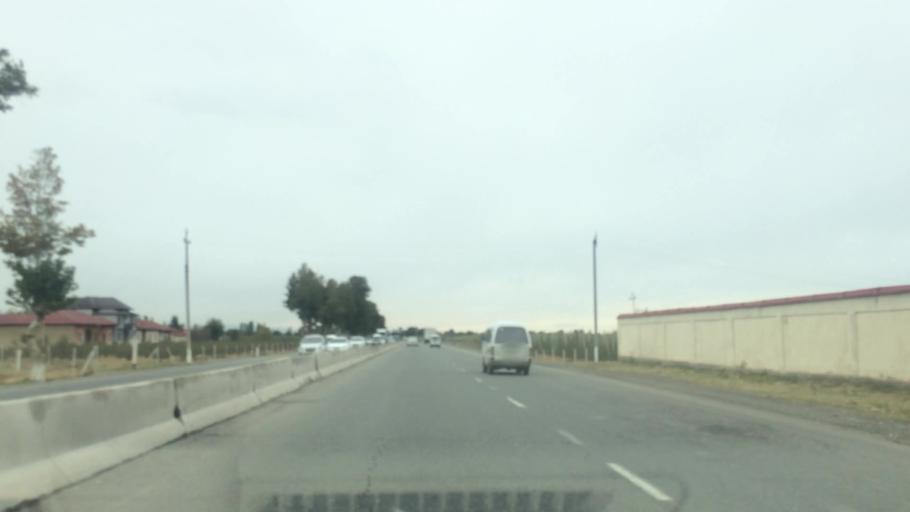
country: UZ
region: Samarqand
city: Jomboy
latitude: 39.7362
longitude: 67.1730
